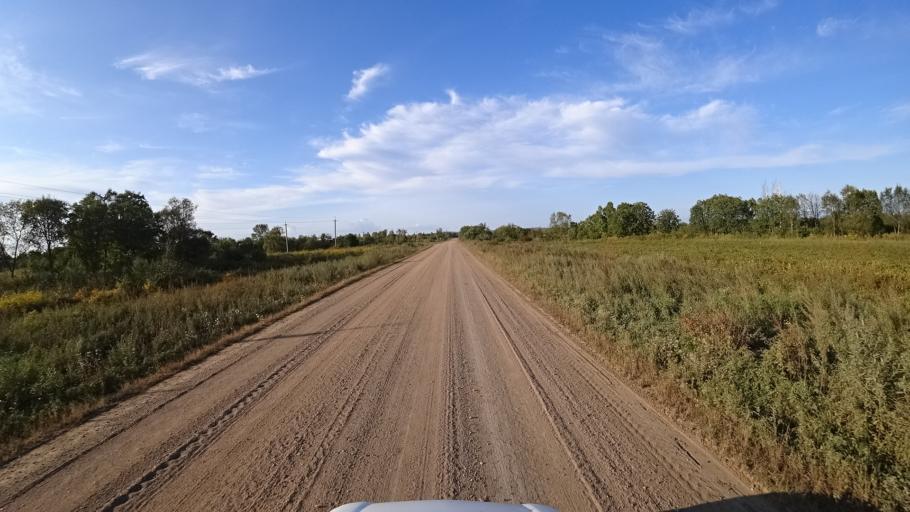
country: RU
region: Amur
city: Arkhara
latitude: 49.3590
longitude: 130.1371
